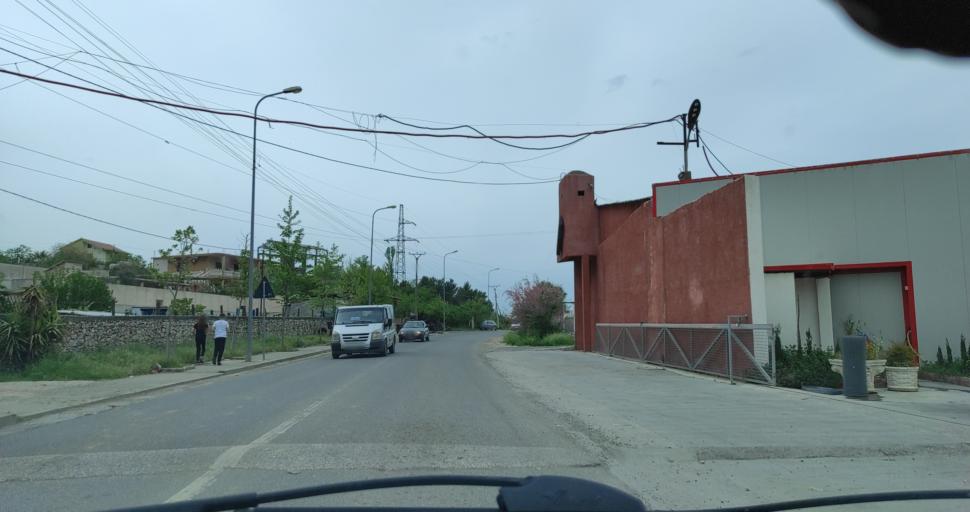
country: AL
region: Lezhe
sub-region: Rrethi i Kurbinit
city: Lac
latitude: 41.6220
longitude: 19.7090
